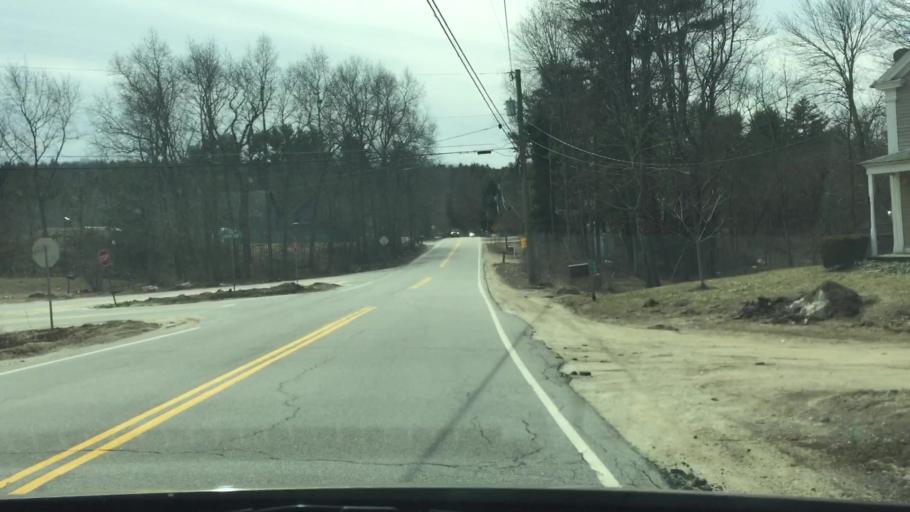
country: US
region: New Hampshire
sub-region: Strafford County
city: Barrington
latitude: 43.2384
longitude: -71.0551
